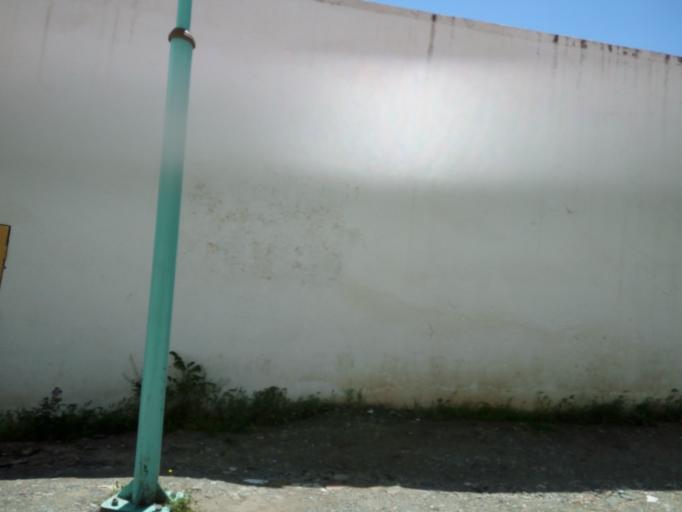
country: DZ
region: Constantine
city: Constantine
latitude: 36.3739
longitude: 6.6178
